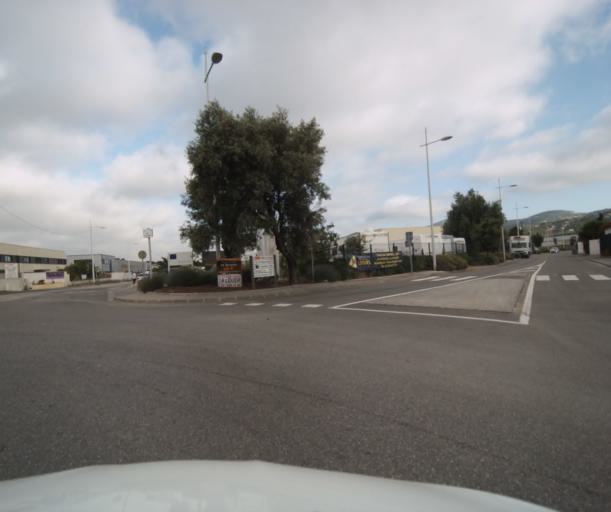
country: FR
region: Provence-Alpes-Cote d'Azur
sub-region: Departement du Var
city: Ollioules
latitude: 43.1175
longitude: 5.8422
